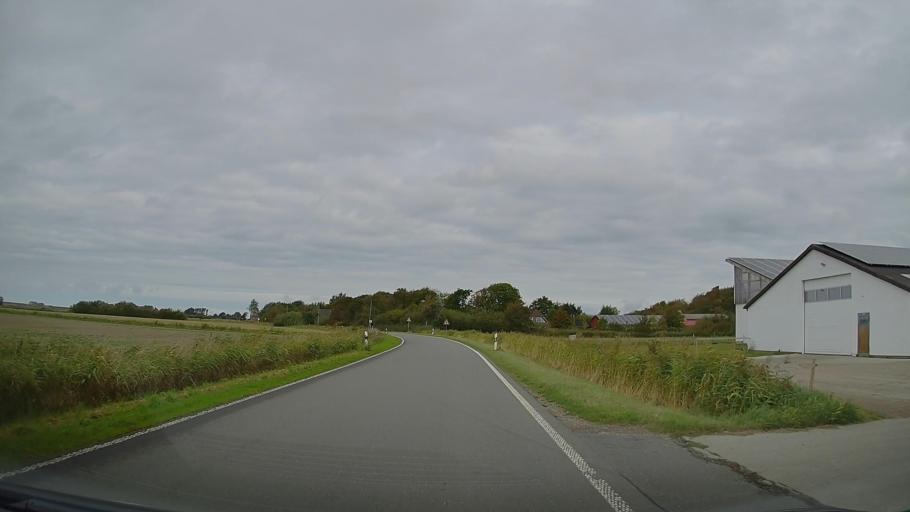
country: DE
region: Schleswig-Holstein
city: Klanxbull
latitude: 54.8746
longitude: 8.6829
